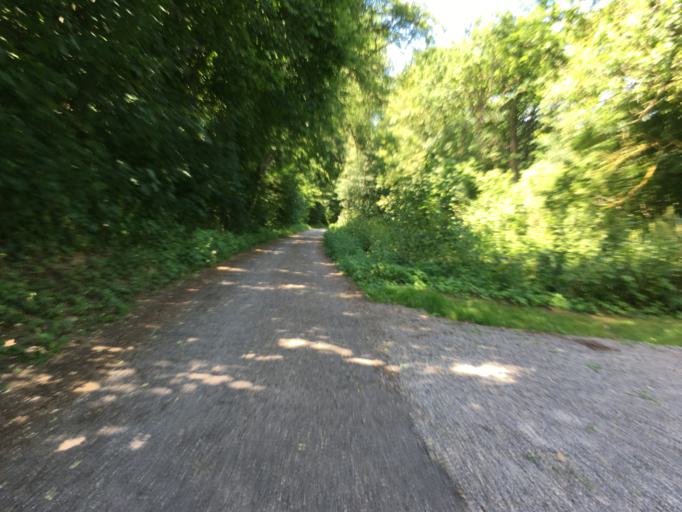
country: DE
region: Baden-Wuerttemberg
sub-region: Regierungsbezirk Stuttgart
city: Vaihingen an der Enz
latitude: 48.9146
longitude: 8.9628
